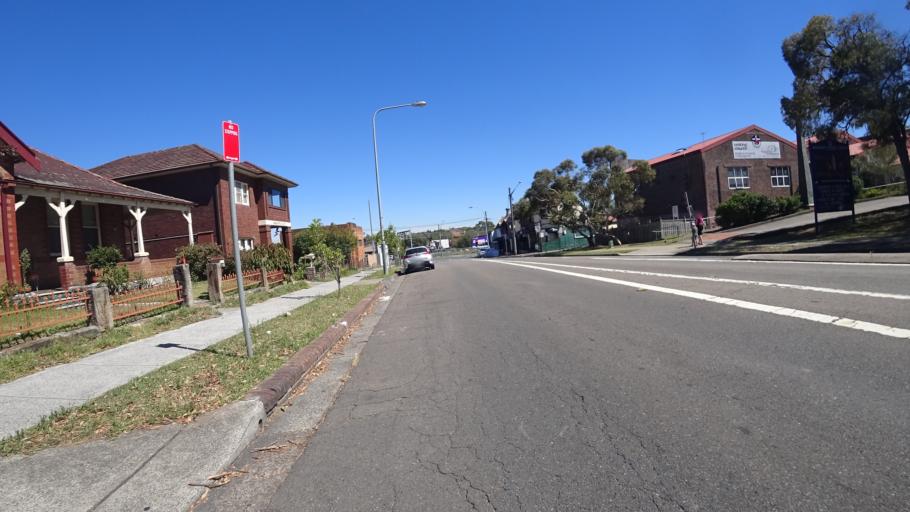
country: AU
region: New South Wales
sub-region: Kogarah
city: Beverly Park
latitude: -33.9666
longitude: 151.1319
